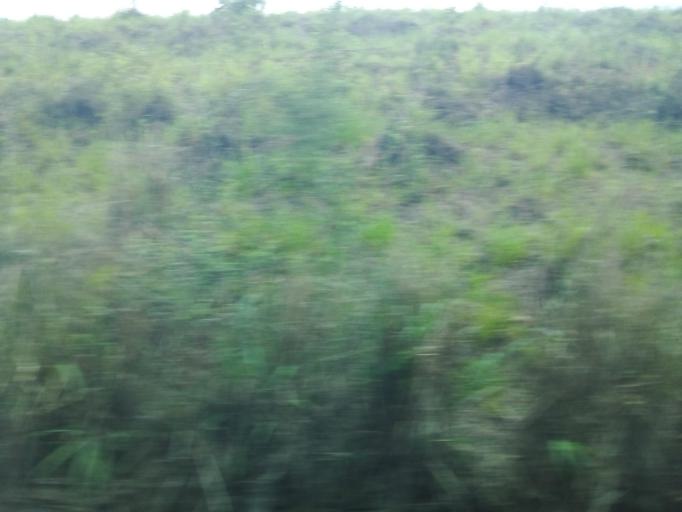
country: BR
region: Minas Gerais
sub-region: Ipatinga
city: Ipatinga
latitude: -19.4634
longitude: -42.4715
